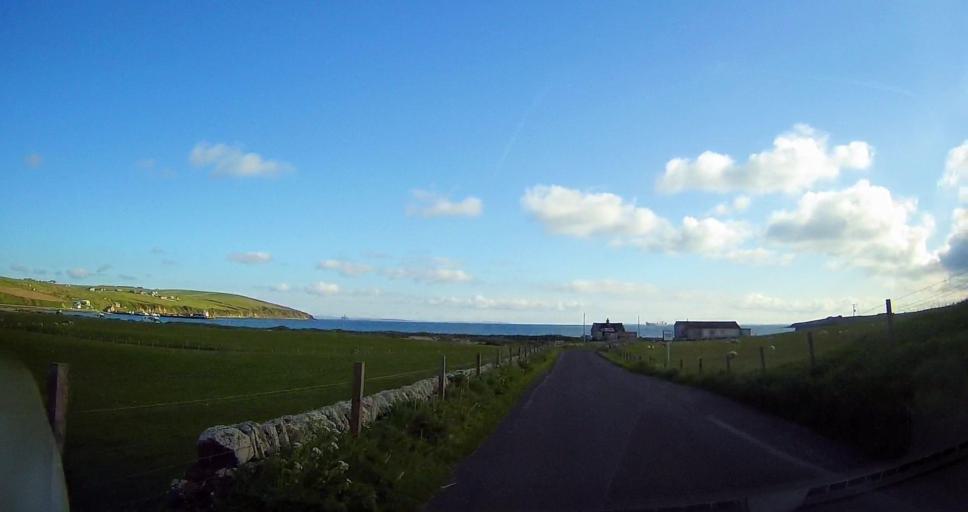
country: GB
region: Scotland
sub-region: Orkney Islands
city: Orkney
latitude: 58.9646
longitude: -2.9779
